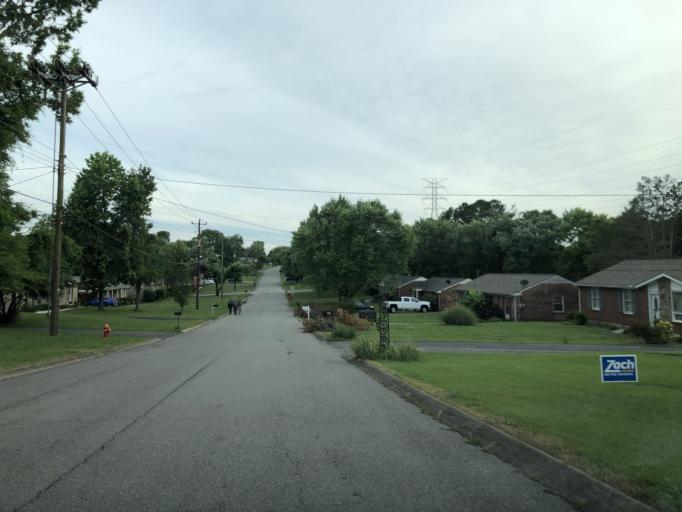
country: US
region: Tennessee
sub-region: Davidson County
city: Goodlettsville
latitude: 36.2959
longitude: -86.7117
